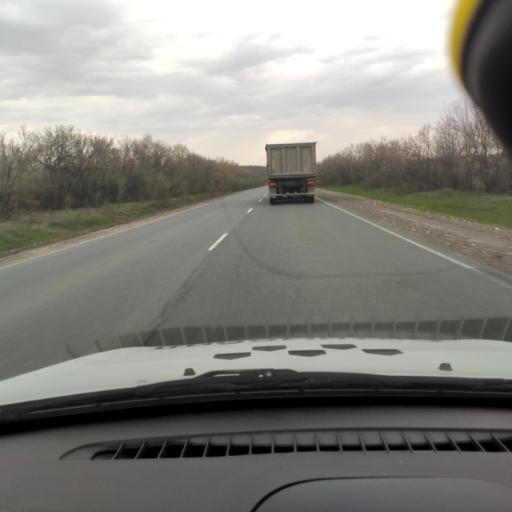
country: RU
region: Samara
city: Zhigulevsk
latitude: 53.3024
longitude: 49.3463
